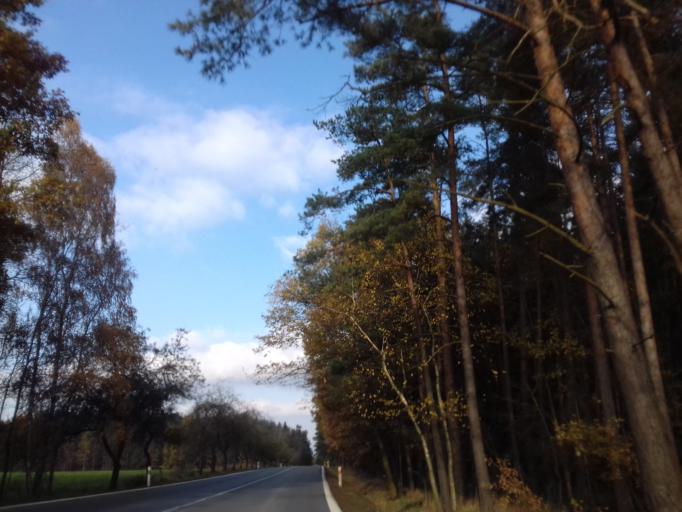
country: CZ
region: Plzensky
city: Meclov
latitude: 49.4749
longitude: 12.8751
